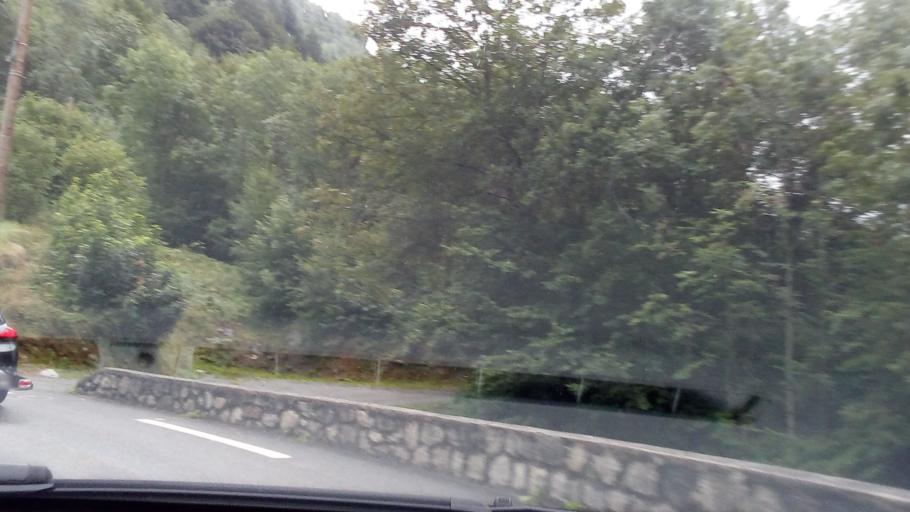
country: FR
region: Midi-Pyrenees
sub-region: Departement des Hautes-Pyrenees
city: Luz-Saint-Sauveur
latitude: 42.8902
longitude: 0.0480
